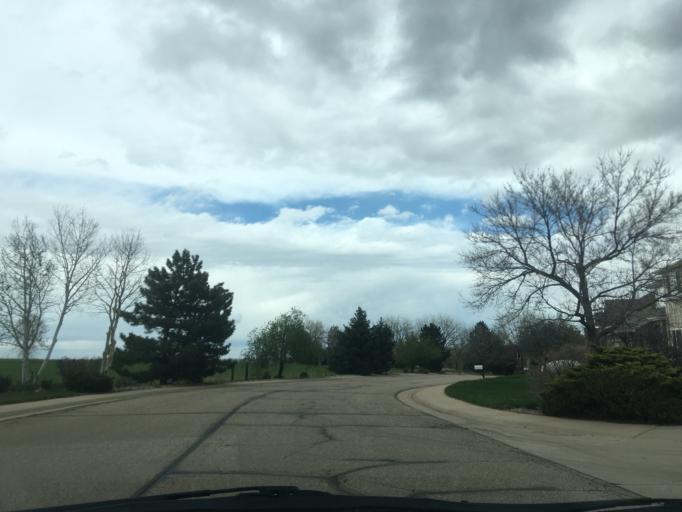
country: US
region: Colorado
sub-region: Boulder County
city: Louisville
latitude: 40.0226
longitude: -105.1289
